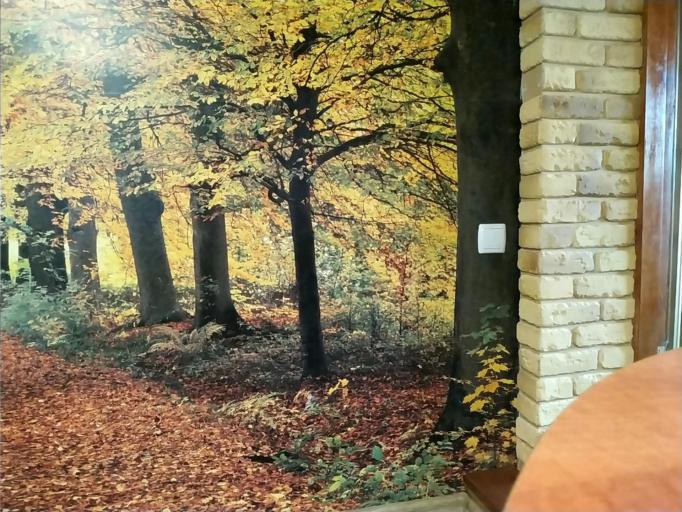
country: RU
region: Leningrad
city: Tolmachevo
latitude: 58.9307
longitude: 29.7170
